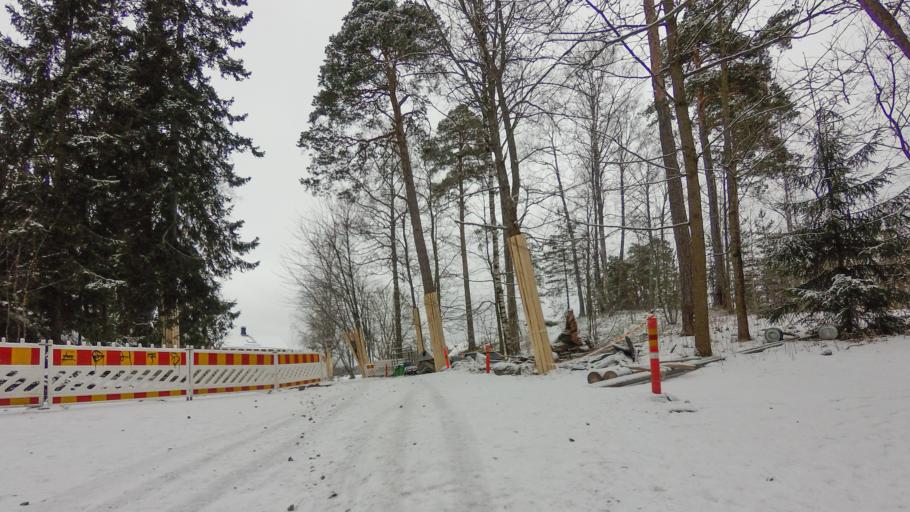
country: FI
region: Uusimaa
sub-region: Helsinki
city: Teekkarikylae
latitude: 60.1853
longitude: 24.8852
